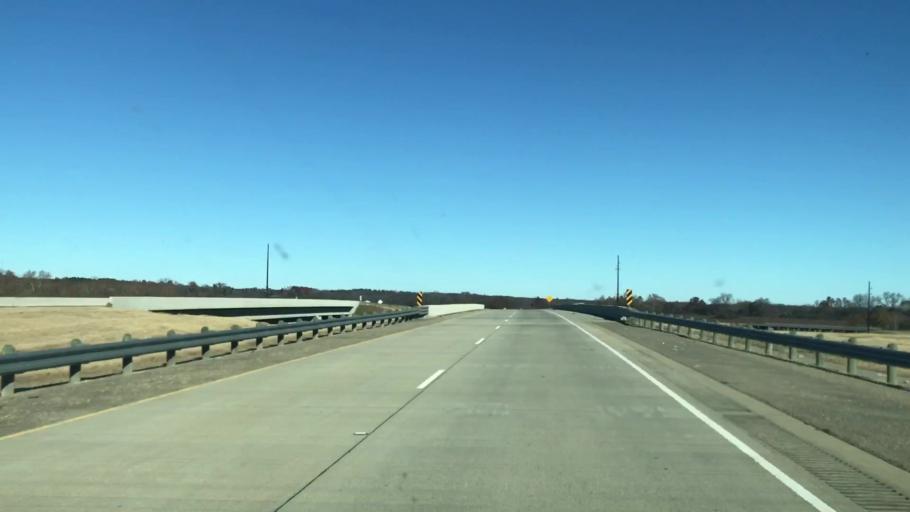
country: US
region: Louisiana
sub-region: Caddo Parish
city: Vivian
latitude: 32.8962
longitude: -93.8610
